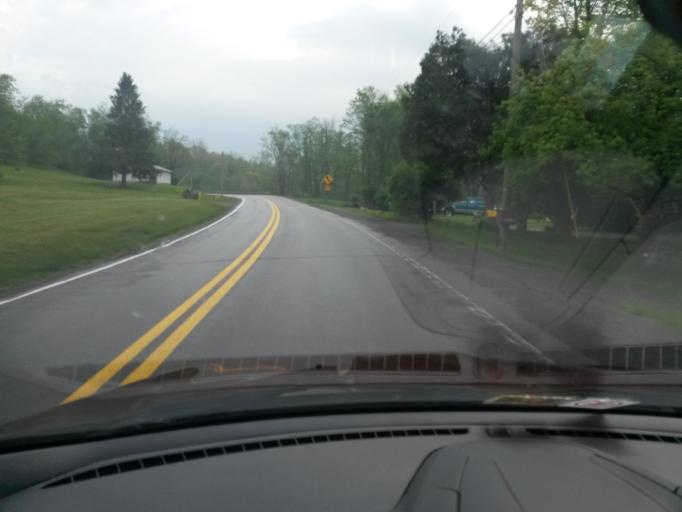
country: US
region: West Virginia
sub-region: Randolph County
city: Elkins
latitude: 38.7840
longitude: -79.9079
